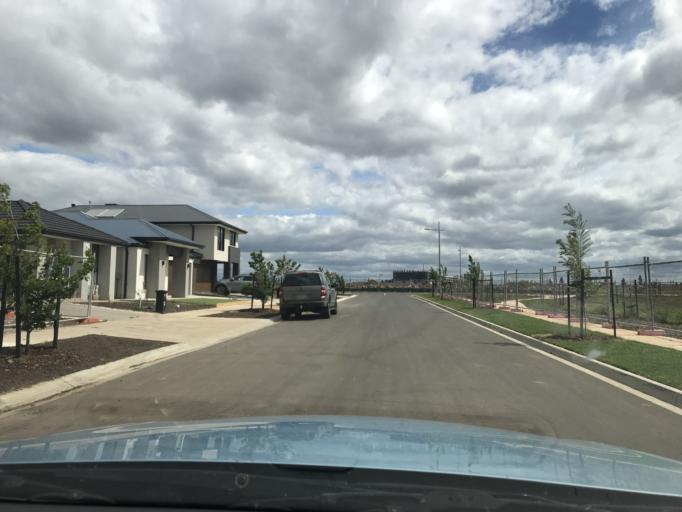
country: AU
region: Victoria
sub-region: Wyndham
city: Williams Landing
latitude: -37.8650
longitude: 144.7539
